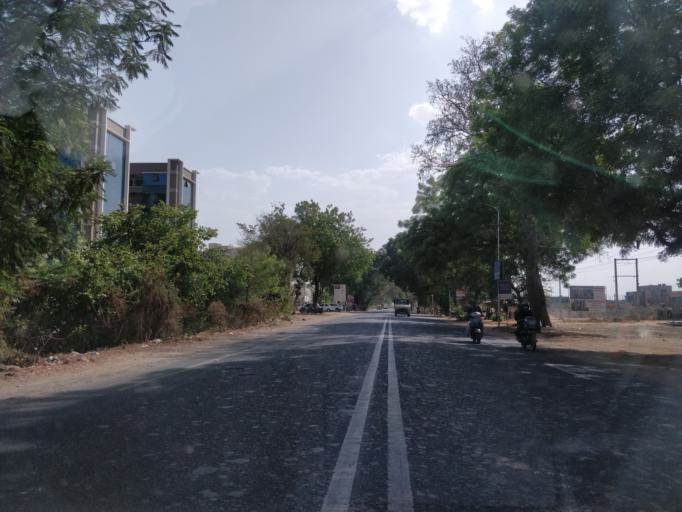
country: IN
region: Gujarat
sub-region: Ahmadabad
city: Naroda
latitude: 23.0871
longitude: 72.6838
